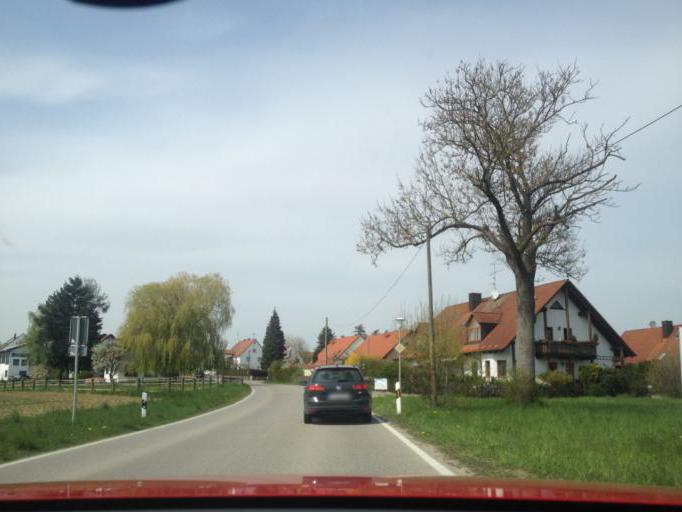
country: DE
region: Bavaria
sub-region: Upper Bavaria
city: Paunzhausen
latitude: 48.4736
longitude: 11.5710
